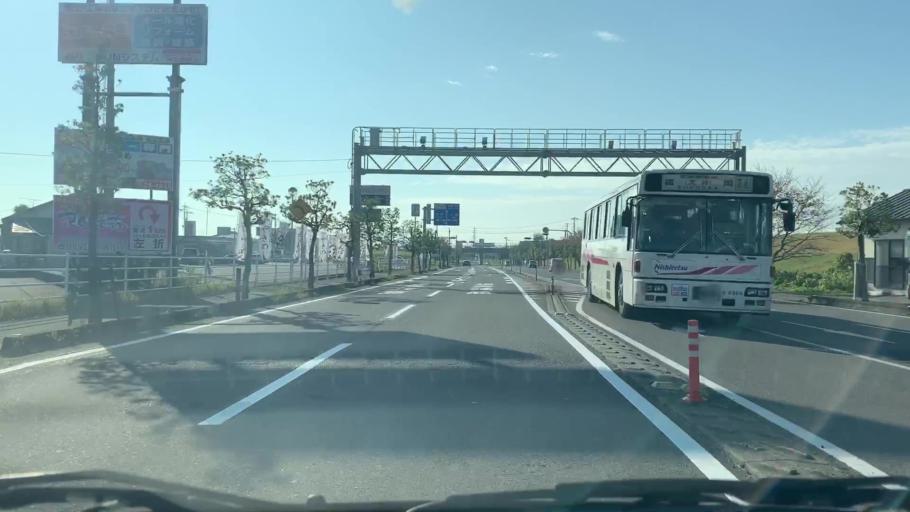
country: JP
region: Saga Prefecture
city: Saga-shi
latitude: 33.3119
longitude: 130.2760
